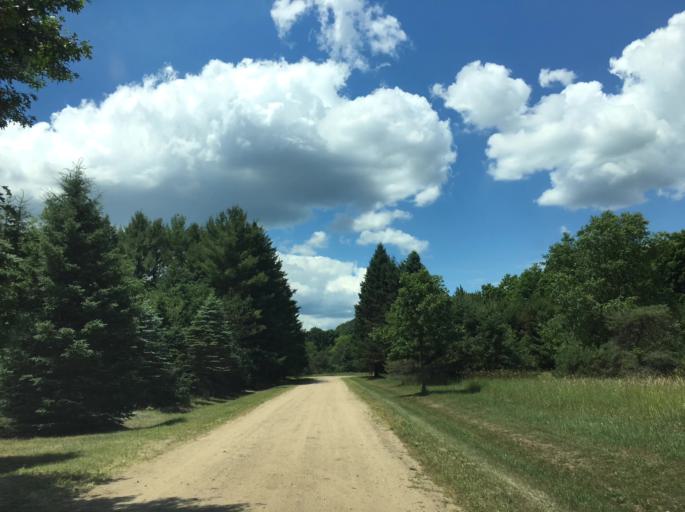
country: US
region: Michigan
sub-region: Osceola County
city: Evart
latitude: 43.8606
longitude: -85.3768
